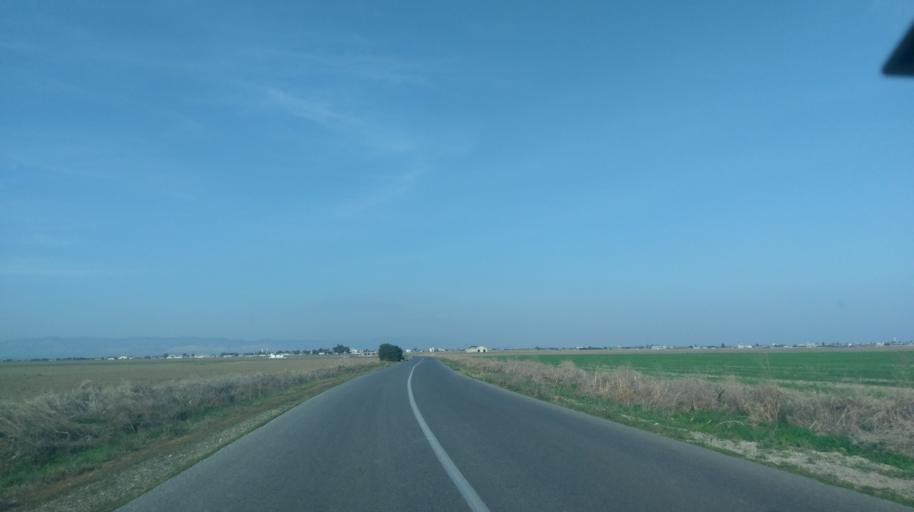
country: CY
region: Ammochostos
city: Achna
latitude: 35.1518
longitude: 33.7499
